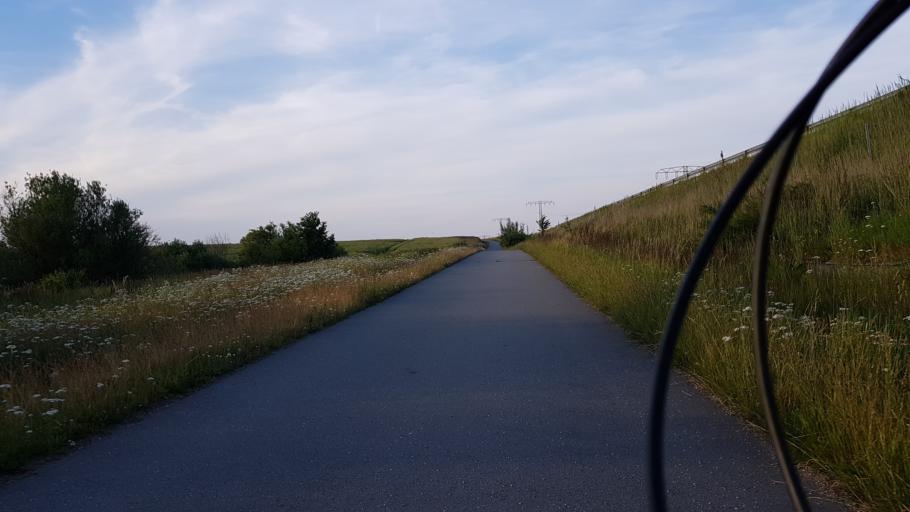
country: DE
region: Mecklenburg-Vorpommern
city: Lankow
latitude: 53.6557
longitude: 11.3513
